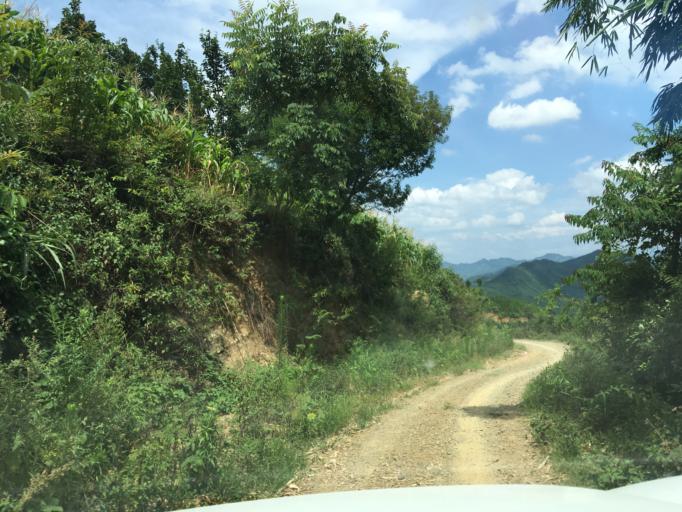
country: CN
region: Guangxi Zhuangzu Zizhiqu
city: Tongle
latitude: 24.9711
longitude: 105.9704
